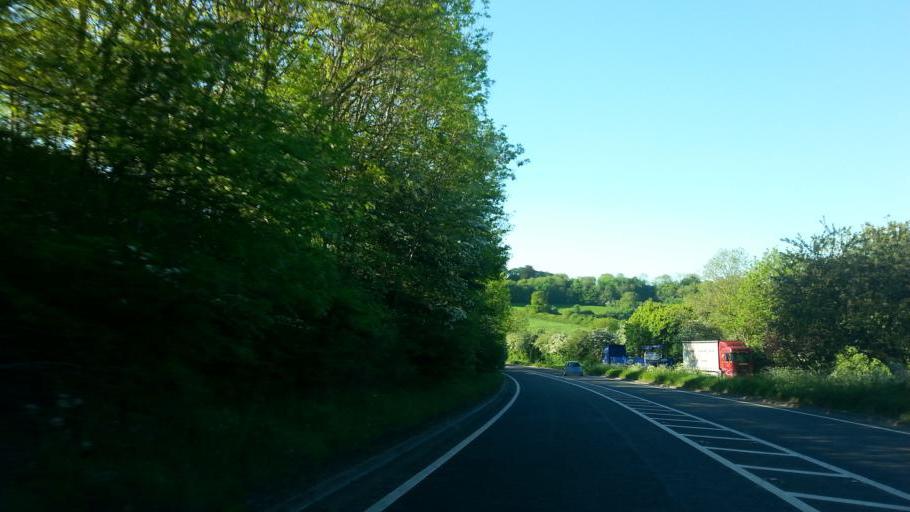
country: GB
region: England
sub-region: Bath and North East Somerset
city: Publow
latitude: 51.3859
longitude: -2.5509
